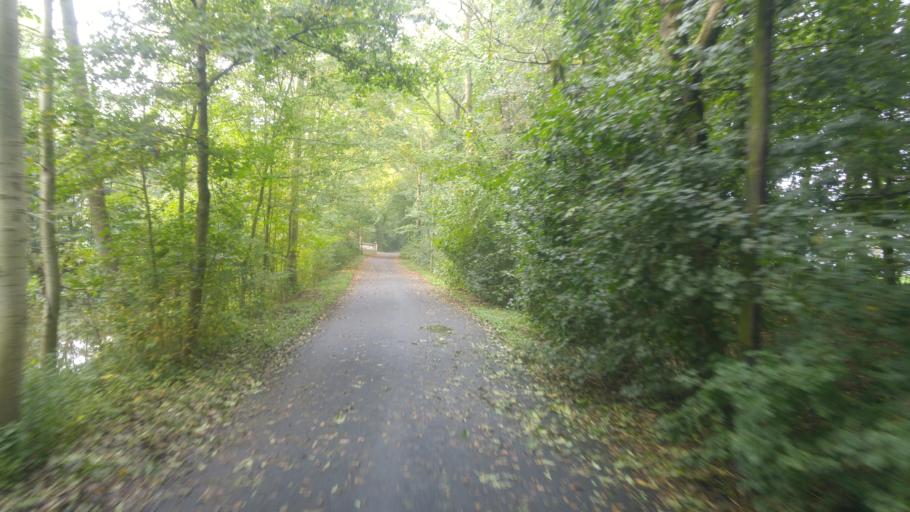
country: DE
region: Bremen
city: Bremen
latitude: 53.1081
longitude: 8.8344
